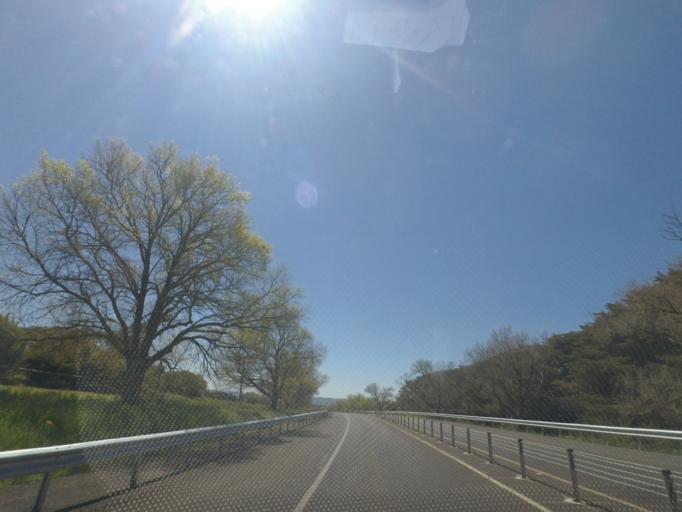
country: AU
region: Victoria
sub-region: Hume
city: Sunbury
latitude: -37.3179
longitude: 144.7407
